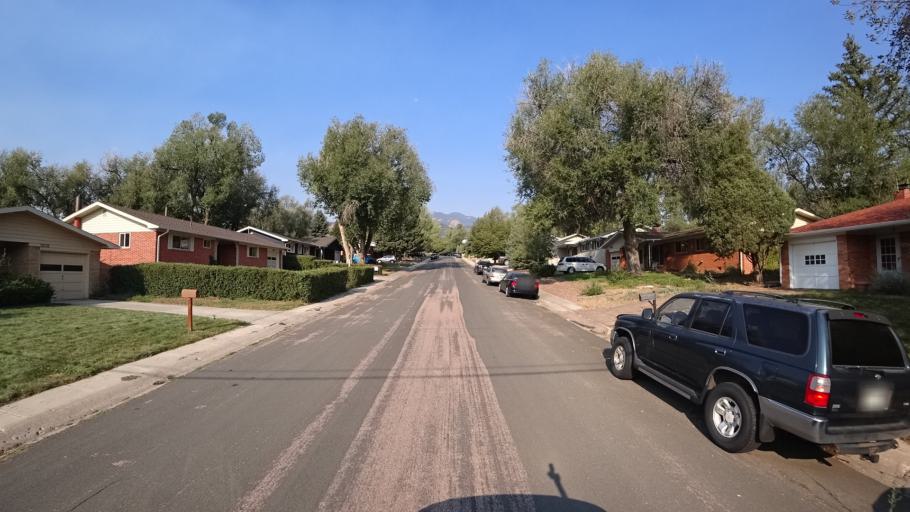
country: US
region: Colorado
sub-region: El Paso County
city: Colorado Springs
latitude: 38.8082
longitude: -104.8465
